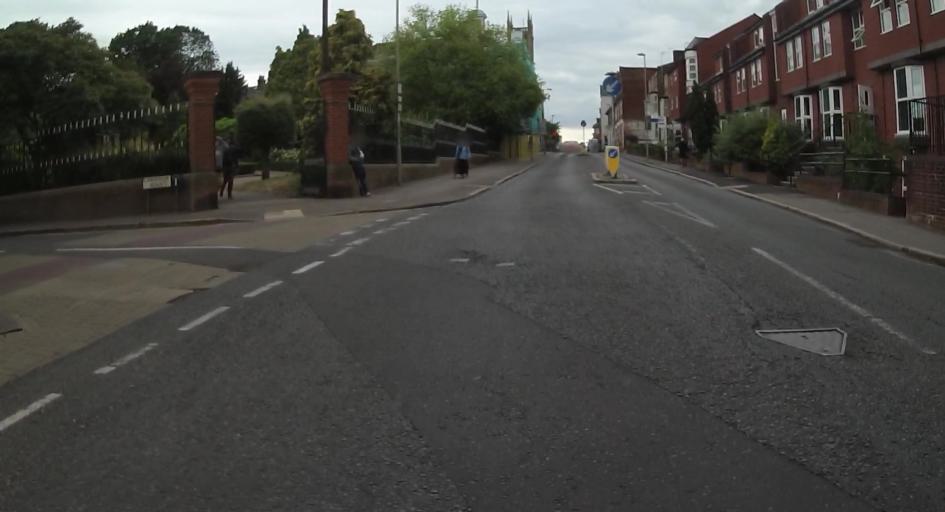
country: GB
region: England
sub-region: Hampshire
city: Aldershot
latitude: 51.2476
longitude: -0.7666
